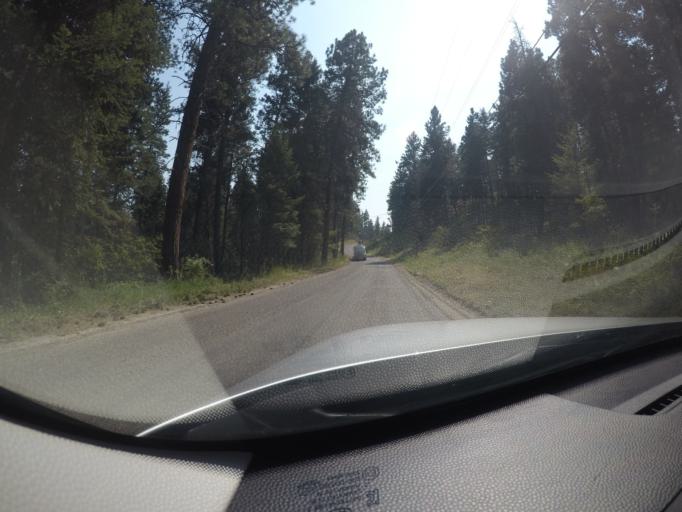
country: US
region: Montana
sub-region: Lake County
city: Polson
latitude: 47.7689
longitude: -114.1518
